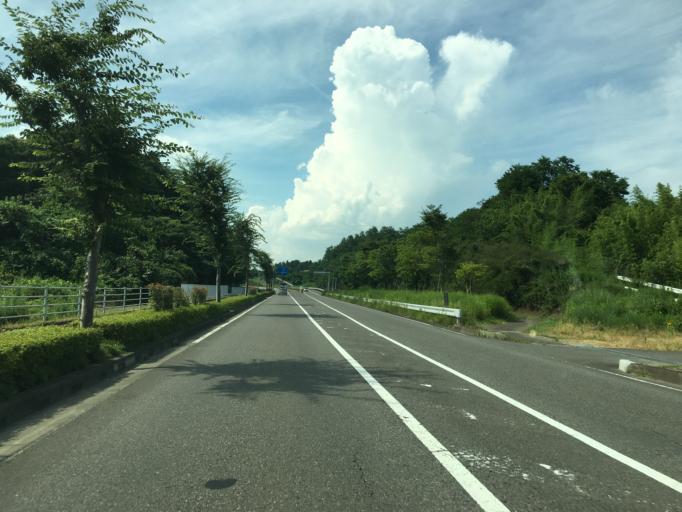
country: JP
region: Fukushima
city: Sukagawa
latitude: 37.2519
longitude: 140.4293
